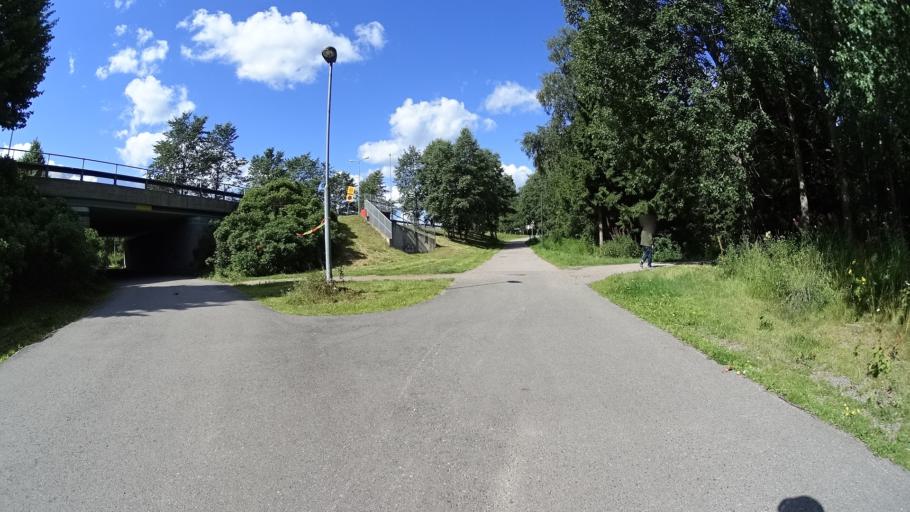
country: FI
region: Uusimaa
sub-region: Helsinki
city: Tuusula
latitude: 60.4036
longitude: 25.0325
